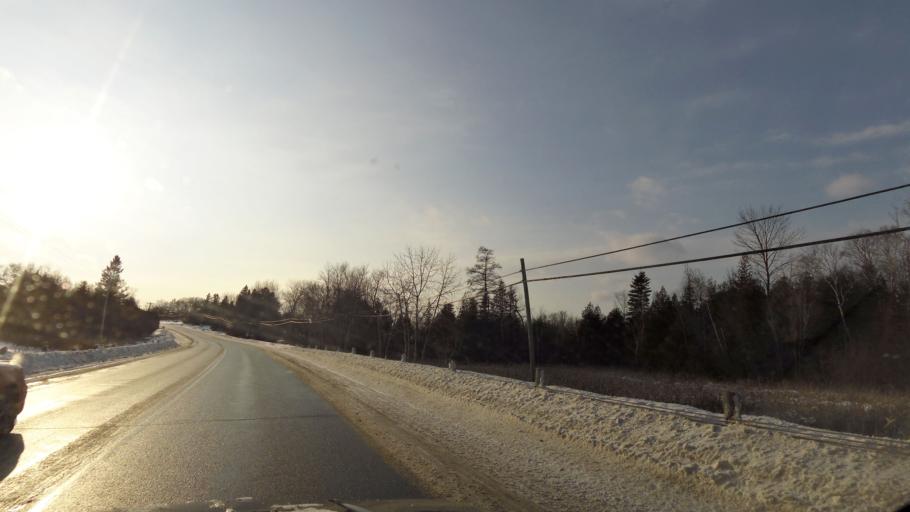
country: CA
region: Ontario
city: Omemee
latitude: 44.5754
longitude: -78.9434
